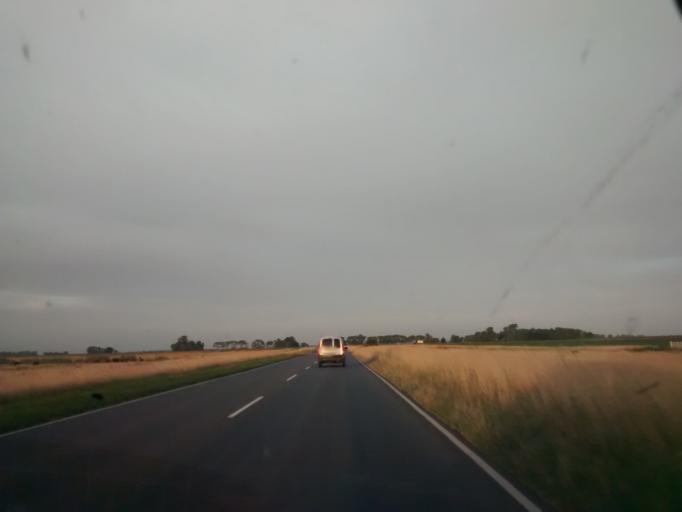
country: AR
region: Buenos Aires
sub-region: Partido de General Belgrano
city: General Belgrano
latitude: -35.8476
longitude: -58.5980
